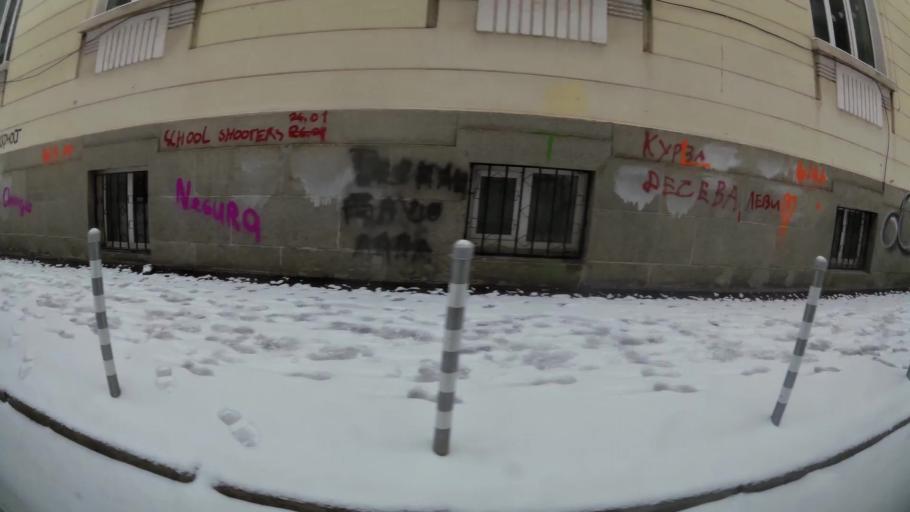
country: BG
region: Sofia-Capital
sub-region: Stolichna Obshtina
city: Sofia
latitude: 42.7014
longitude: 23.3115
